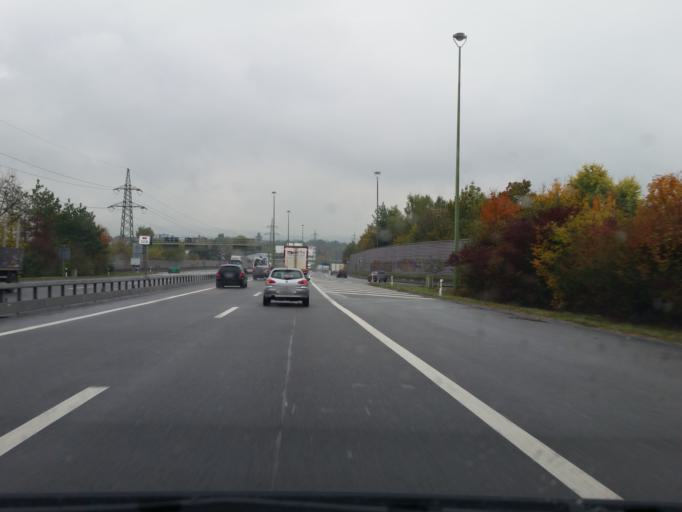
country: CH
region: Zurich
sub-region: Bezirk Uster
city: Bruttisellen
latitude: 47.4166
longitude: 8.6281
